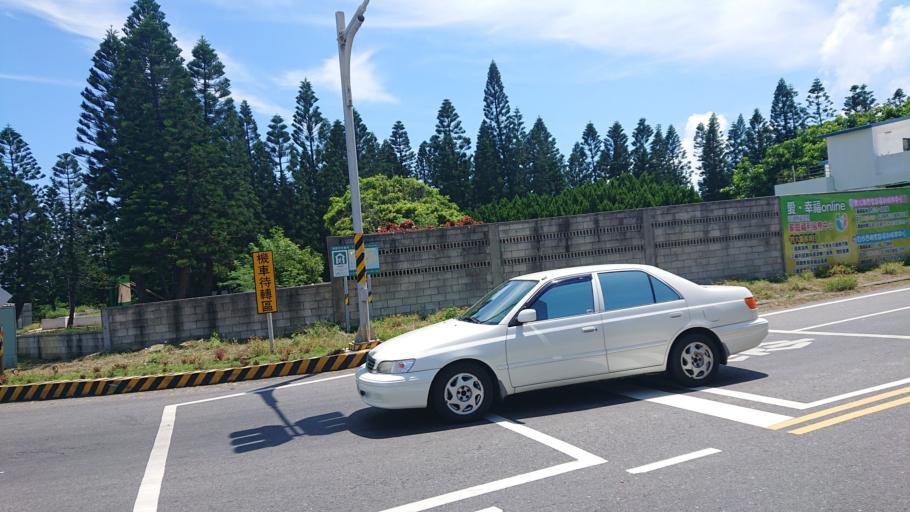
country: TW
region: Taiwan
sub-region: Penghu
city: Ma-kung
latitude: 23.6439
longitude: 119.5976
